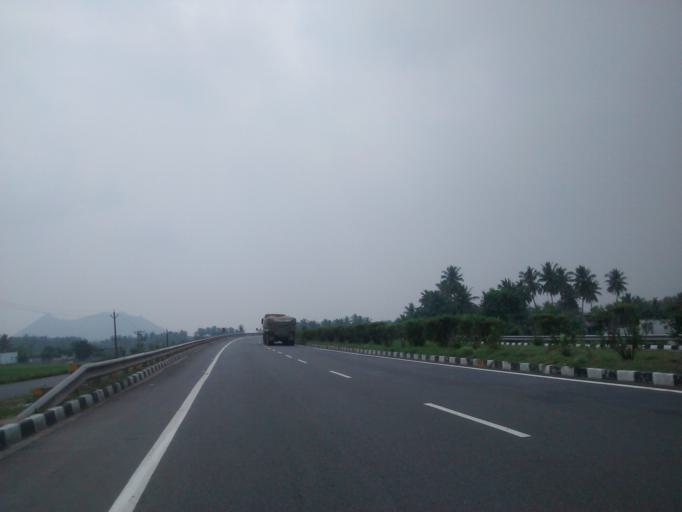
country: IN
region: Tamil Nadu
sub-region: Krishnagiri
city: Kaverippattanam
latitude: 12.4084
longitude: 78.2237
